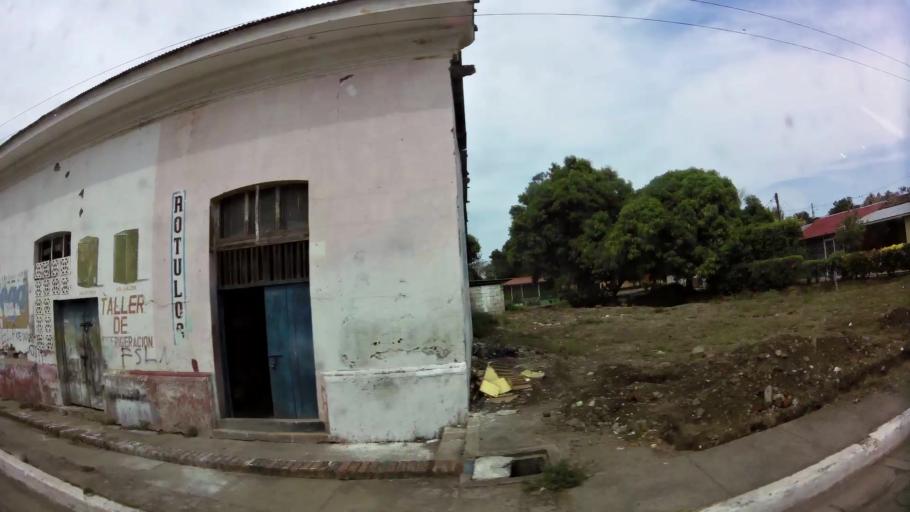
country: NI
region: Rivas
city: Rivas
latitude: 11.4363
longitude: -85.8288
